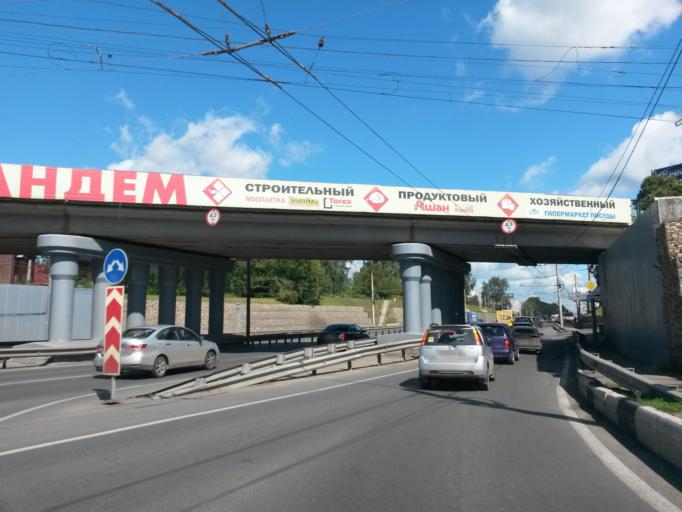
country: RU
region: Jaroslavl
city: Yaroslavl
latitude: 57.6018
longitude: 39.8772
